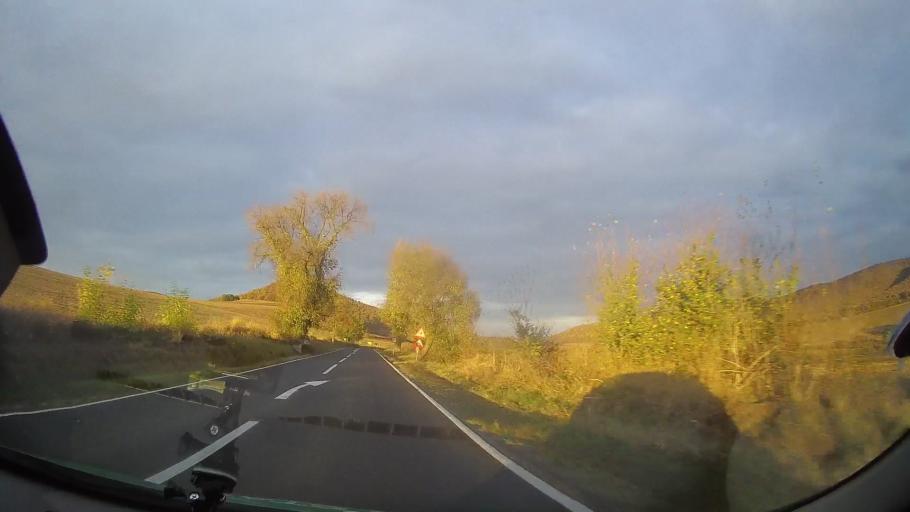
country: RO
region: Tulcea
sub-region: Comuna Ciucurova
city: Ciucurova
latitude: 44.9440
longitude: 28.4958
